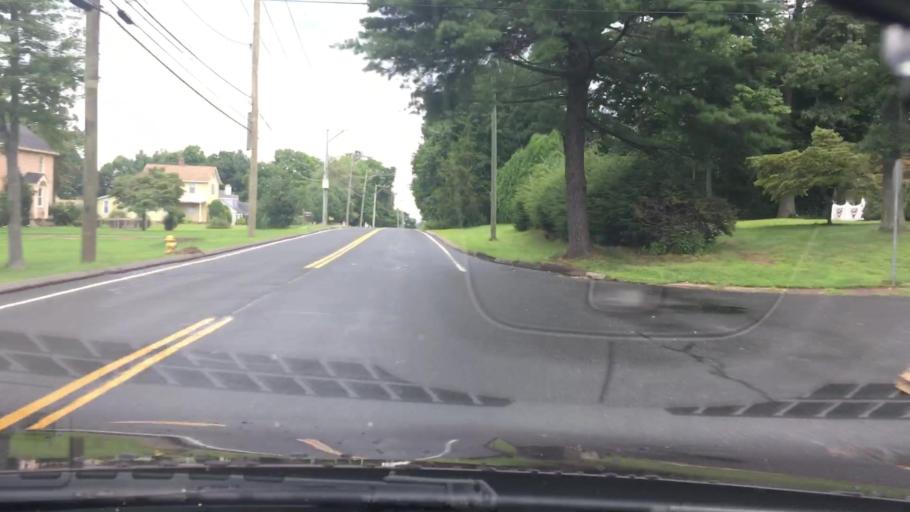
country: US
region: Connecticut
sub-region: Hartford County
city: Manchester
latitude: 41.7439
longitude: -72.5381
